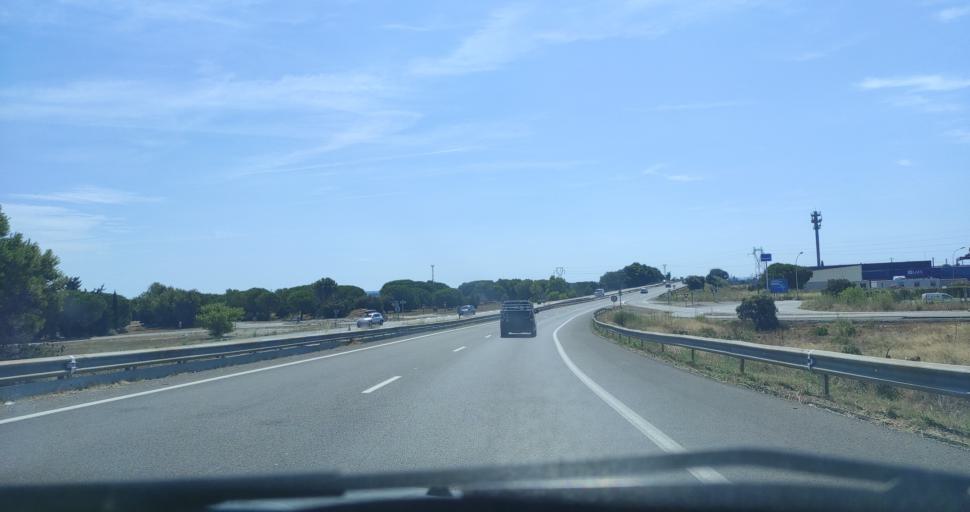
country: FR
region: Provence-Alpes-Cote d'Azur
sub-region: Departement des Bouches-du-Rhone
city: Fos-sur-Mer
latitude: 43.4774
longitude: 4.8974
